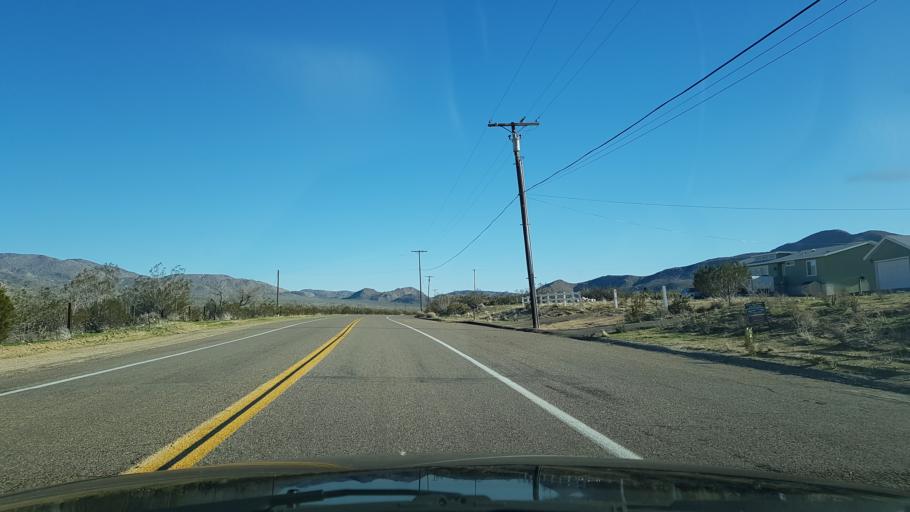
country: US
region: California
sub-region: San Diego County
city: Julian
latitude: 33.0737
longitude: -116.4344
